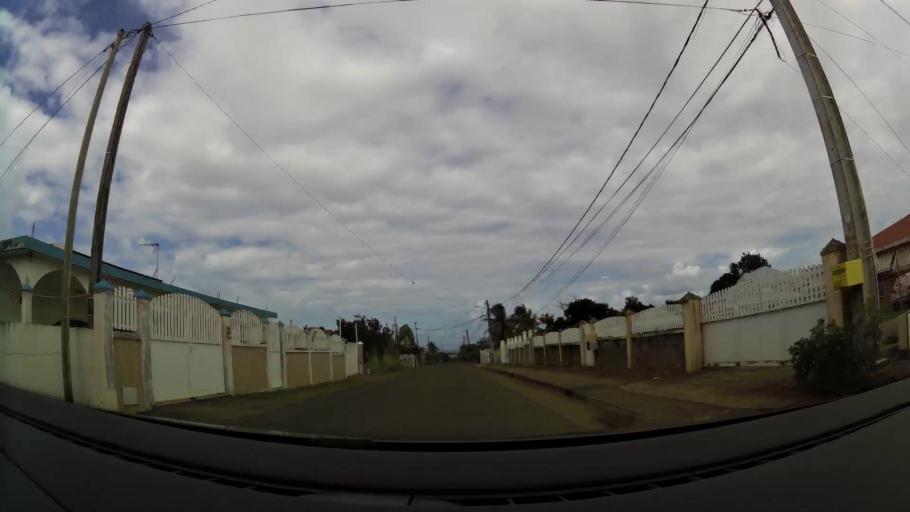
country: GP
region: Guadeloupe
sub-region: Guadeloupe
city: Sainte-Rose
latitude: 16.3250
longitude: -61.6947
